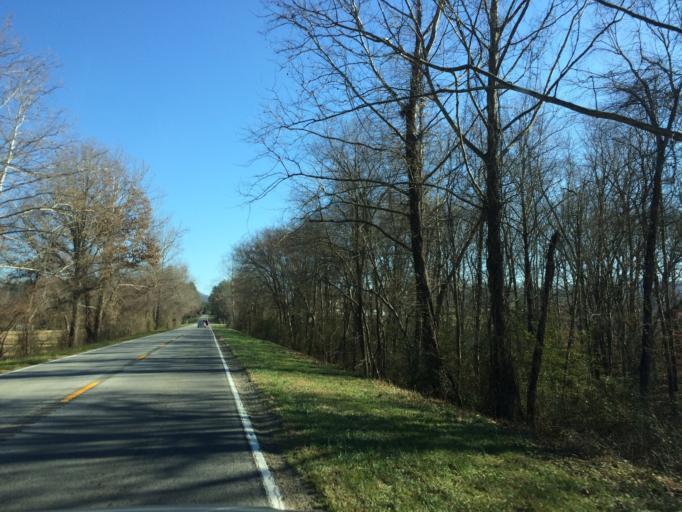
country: US
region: North Carolina
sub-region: Henderson County
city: Mills River
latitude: 35.3724
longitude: -82.5347
